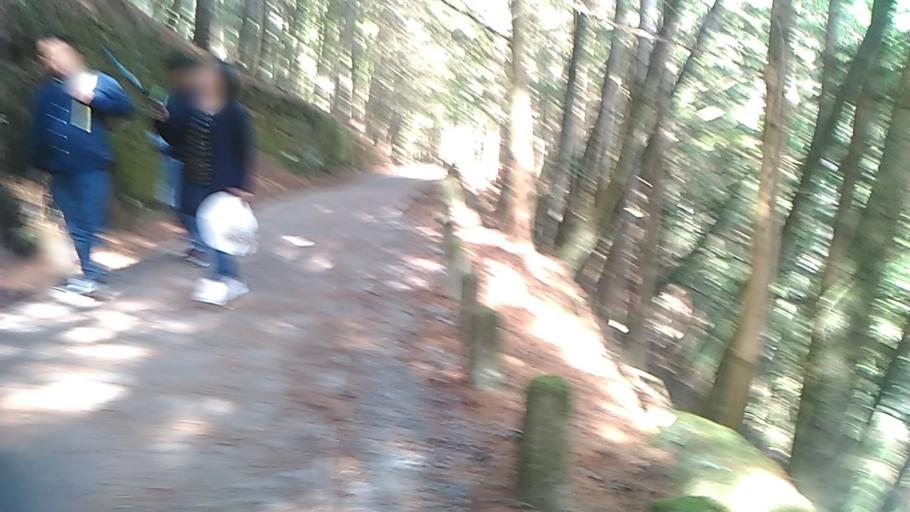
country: TW
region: Taiwan
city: Daxi
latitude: 24.4017
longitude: 121.3069
